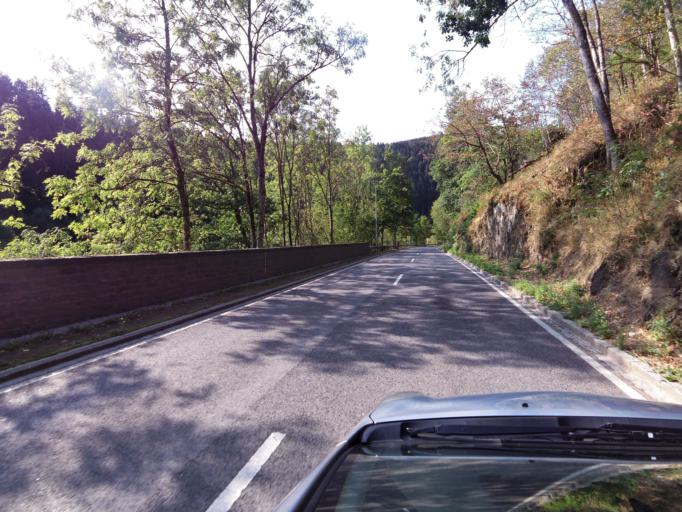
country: LU
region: Diekirch
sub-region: Canton de Wiltz
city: Esch-sur-Sure
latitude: 49.9085
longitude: 5.9435
